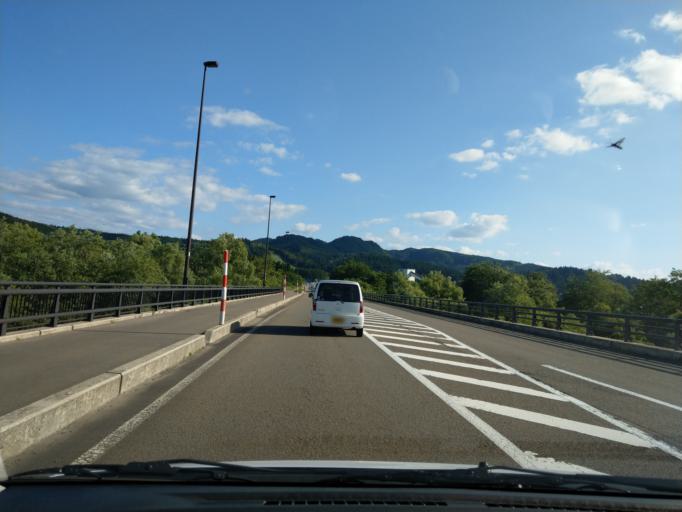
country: JP
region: Akita
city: Takanosu
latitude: 40.1267
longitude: 140.3804
